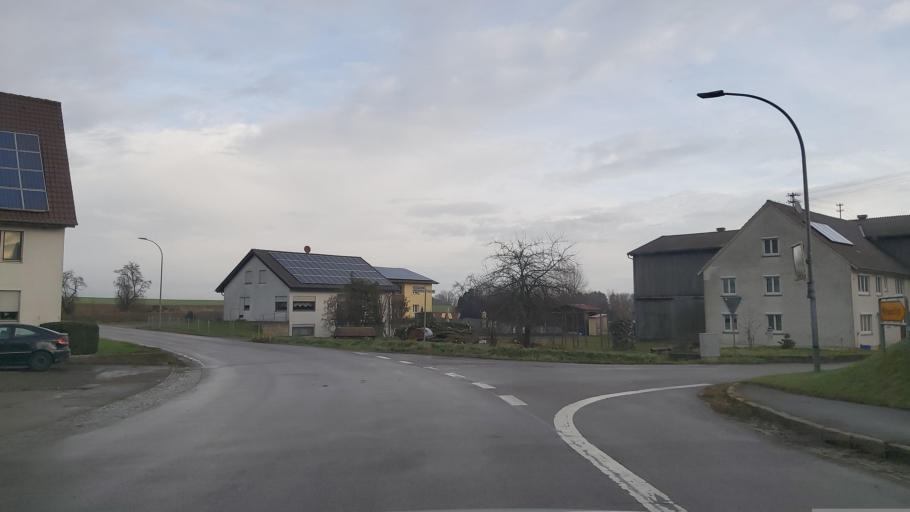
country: DE
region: Baden-Wuerttemberg
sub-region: Tuebingen Region
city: Warthausen
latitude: 48.1494
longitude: 9.7834
